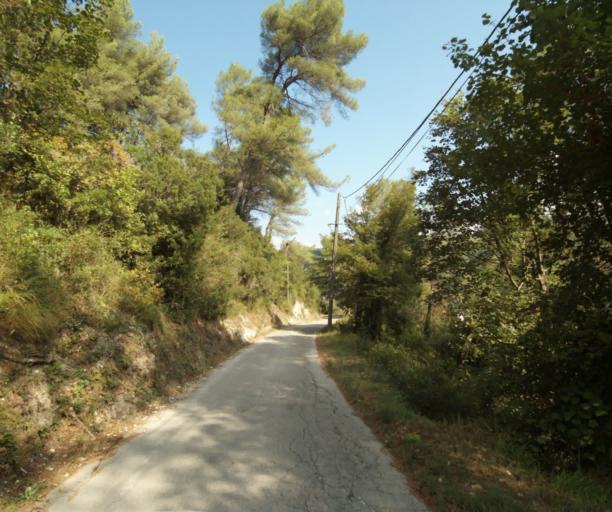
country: FR
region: Provence-Alpes-Cote d'Azur
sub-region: Departement des Alpes-Maritimes
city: Drap
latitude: 43.7626
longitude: 7.3445
